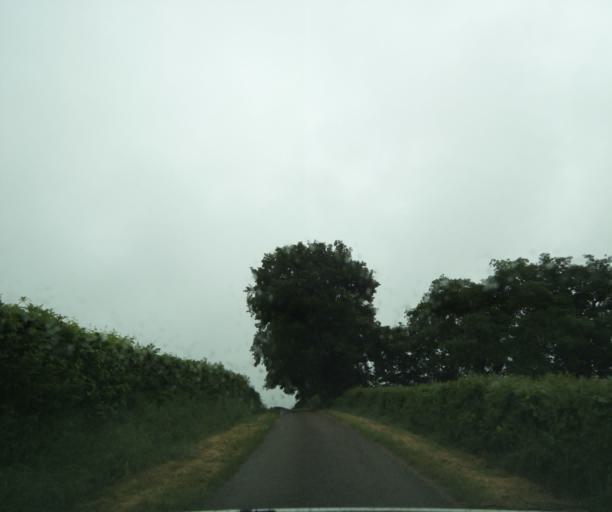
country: FR
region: Bourgogne
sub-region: Departement de Saone-et-Loire
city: Charolles
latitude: 46.4578
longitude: 4.4154
